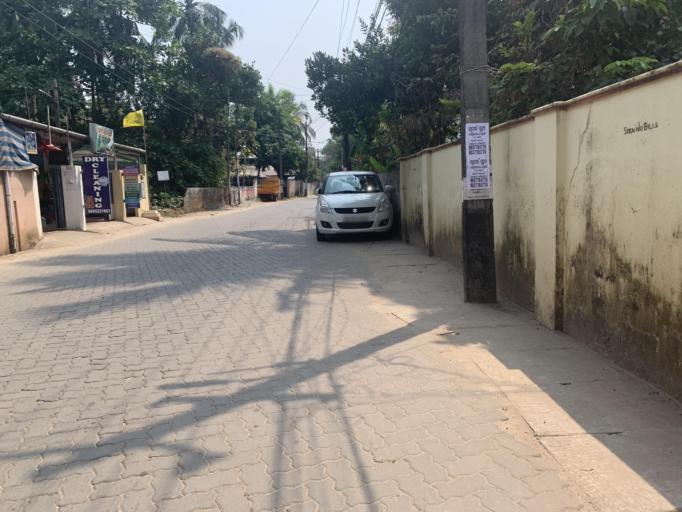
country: IN
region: Kerala
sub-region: Ernakulam
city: Cochin
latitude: 9.9357
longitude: 76.3098
